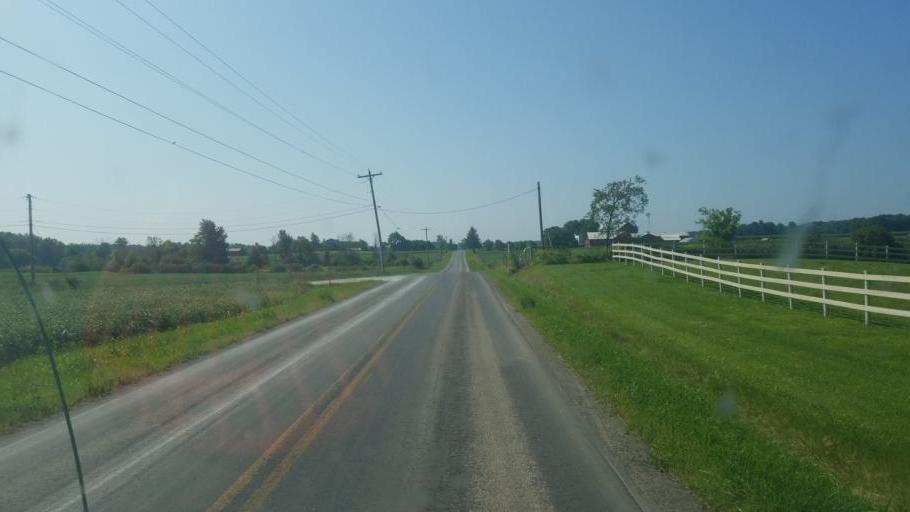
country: US
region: Ohio
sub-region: Wayne County
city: West Salem
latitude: 41.0077
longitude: -82.1641
